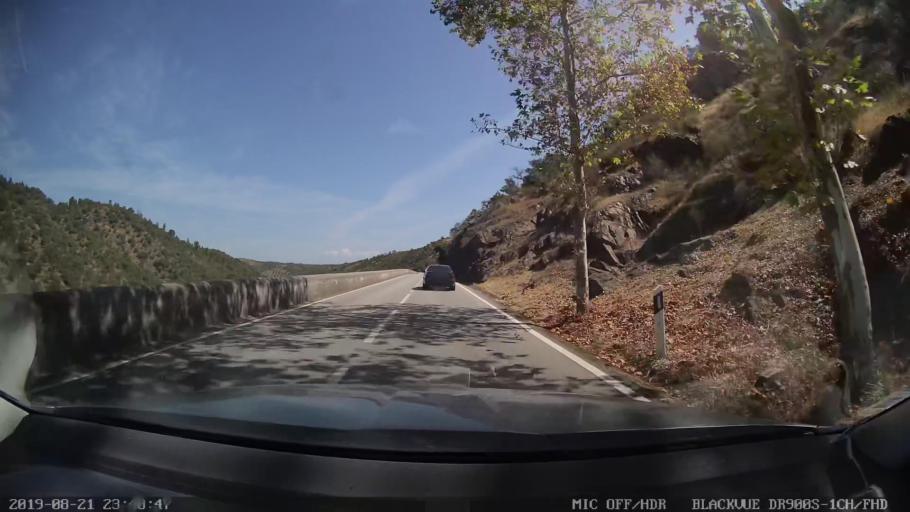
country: PT
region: Castelo Branco
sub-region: Idanha-A-Nova
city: Idanha-a-Nova
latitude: 39.8627
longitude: -7.3289
